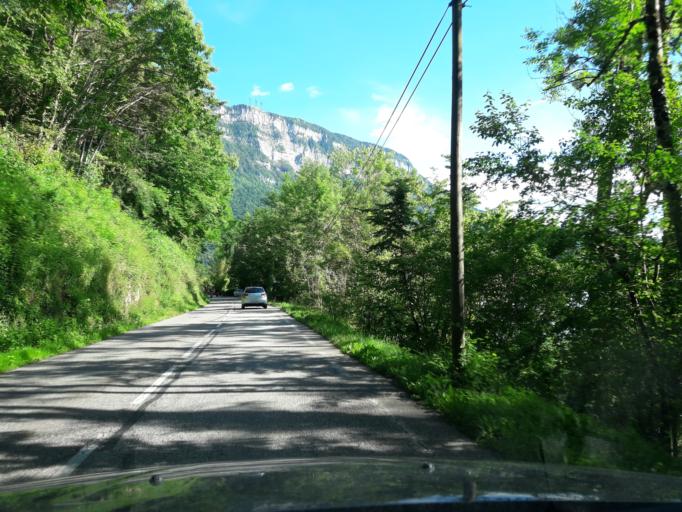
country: FR
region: Rhone-Alpes
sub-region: Departement de la Savoie
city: Vimines
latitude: 45.5499
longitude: 5.8100
